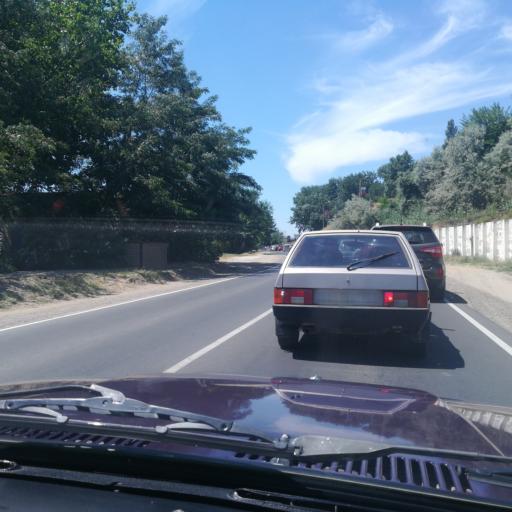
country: RU
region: Krasnodarskiy
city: Vityazevo
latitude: 44.9752
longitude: 37.2761
